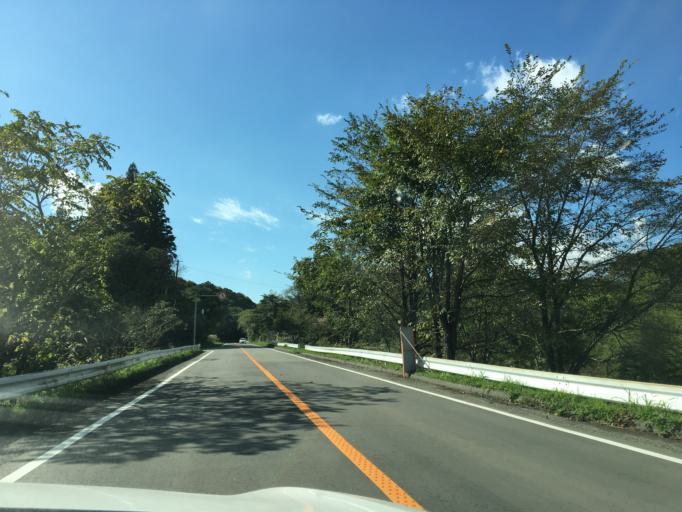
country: JP
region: Fukushima
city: Funehikimachi-funehiki
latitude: 37.5586
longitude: 140.7592
